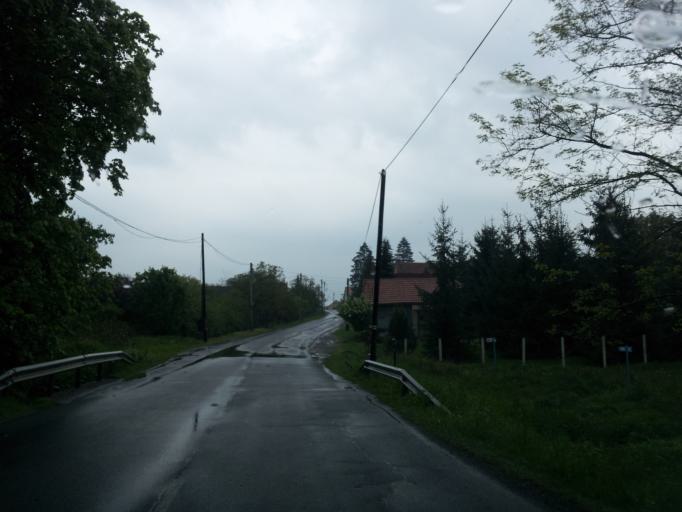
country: HU
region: Baranya
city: Hosszuheteny
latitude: 46.1820
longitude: 18.3194
